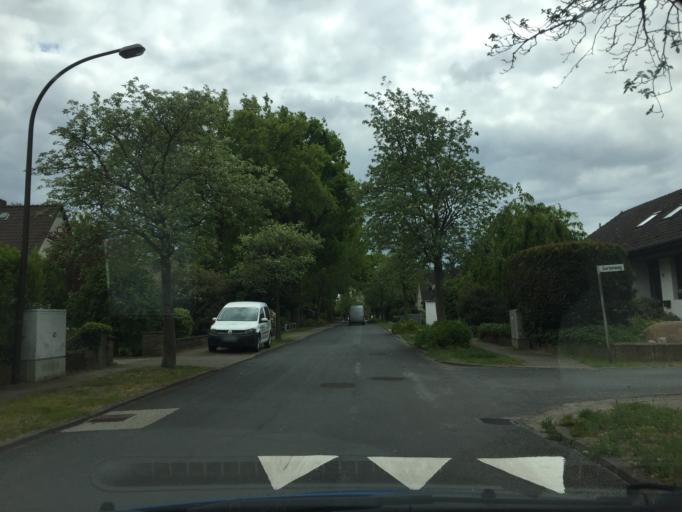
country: DE
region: Lower Saxony
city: Wrestedt
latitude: 52.9266
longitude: 10.5311
